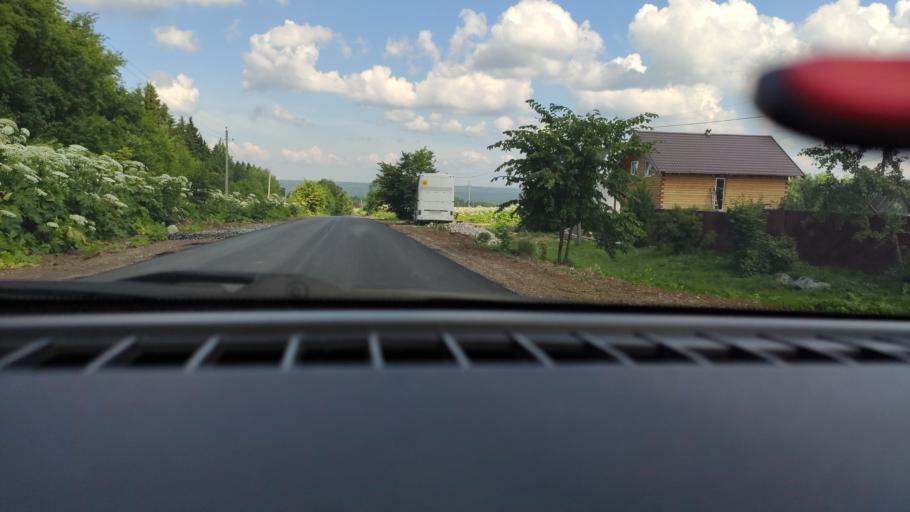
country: RU
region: Perm
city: Sylva
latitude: 58.0340
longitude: 56.7230
